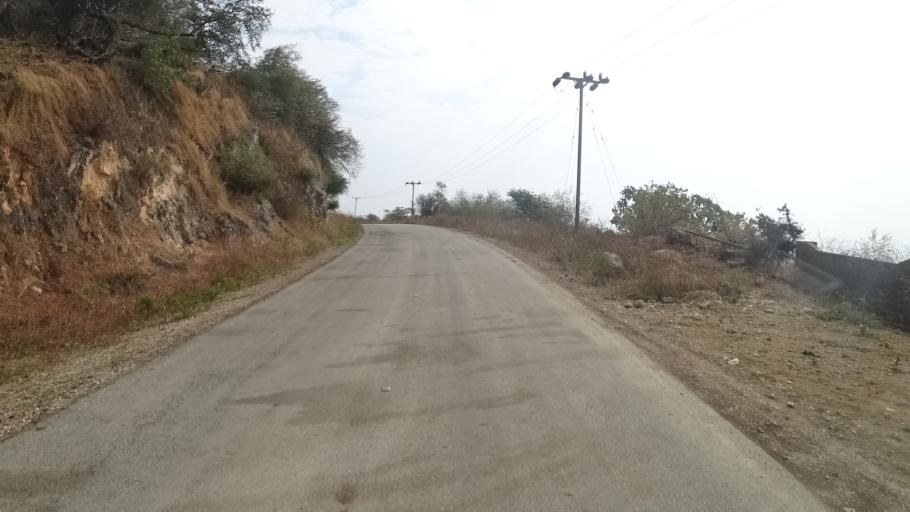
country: YE
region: Al Mahrah
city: Hawf
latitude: 16.7072
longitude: 53.2179
